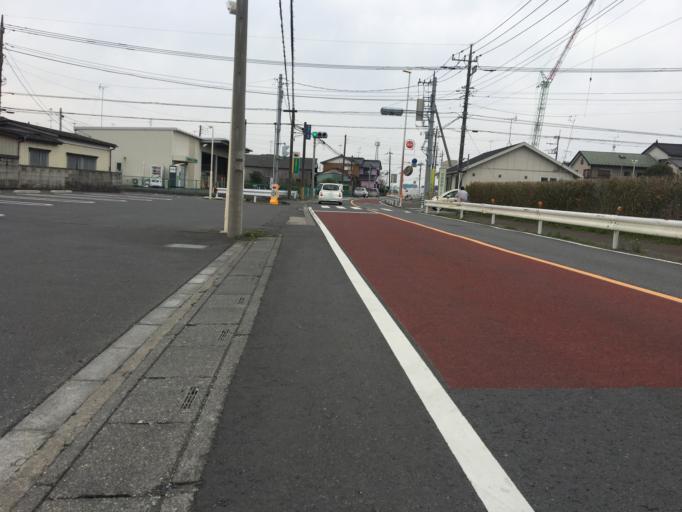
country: JP
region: Saitama
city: Kazo
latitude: 36.1195
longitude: 139.5975
